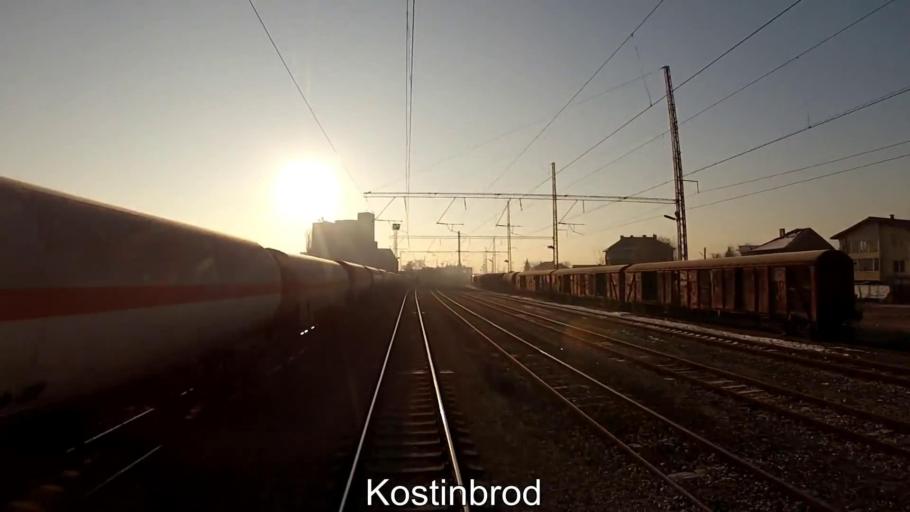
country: BG
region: Sofiya
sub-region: Obshtina Kostinbrod
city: Kostinbrod
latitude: 42.8005
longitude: 23.2043
